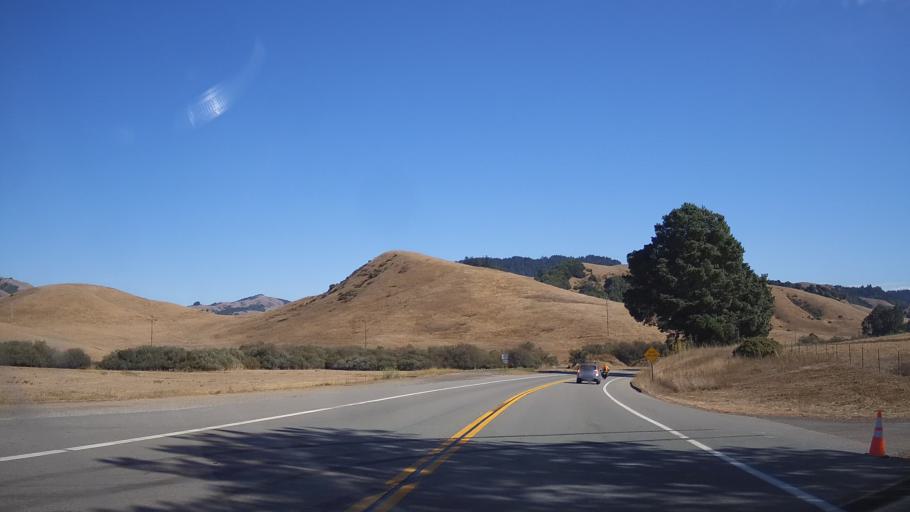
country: US
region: California
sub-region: Marin County
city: Lagunitas-Forest Knolls
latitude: 38.0784
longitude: -122.7101
